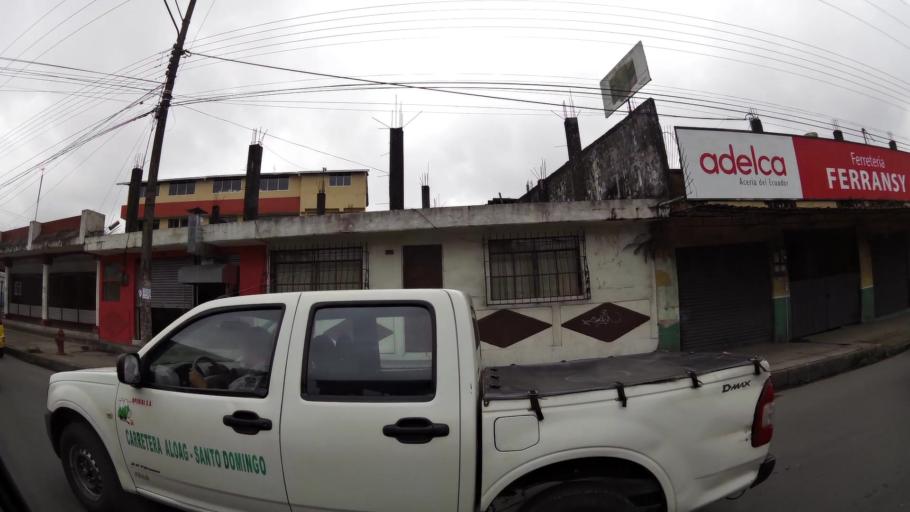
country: EC
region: Santo Domingo de los Tsachilas
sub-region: Canton Santo Domingo de los Colorados
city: Santo Domingo de los Colorados
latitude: -0.2476
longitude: -79.1744
